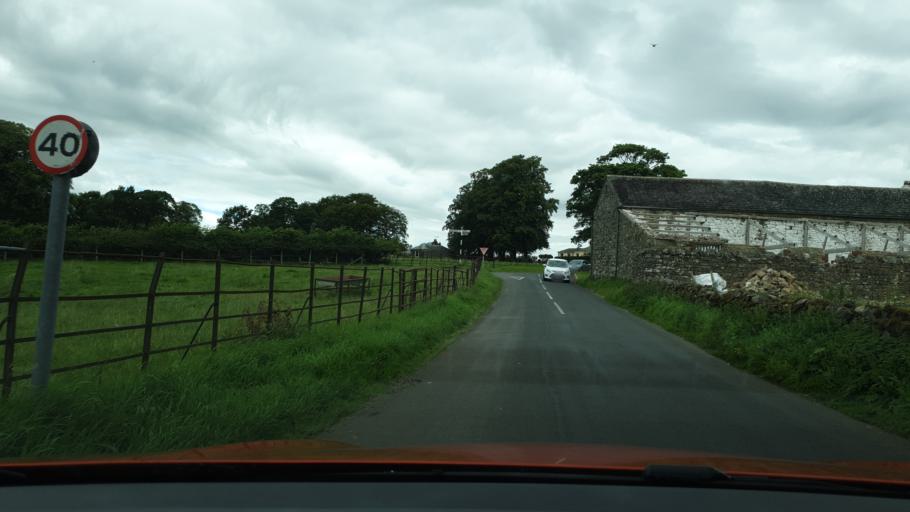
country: GB
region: England
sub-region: Cumbria
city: Penrith
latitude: 54.6132
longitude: -2.8137
